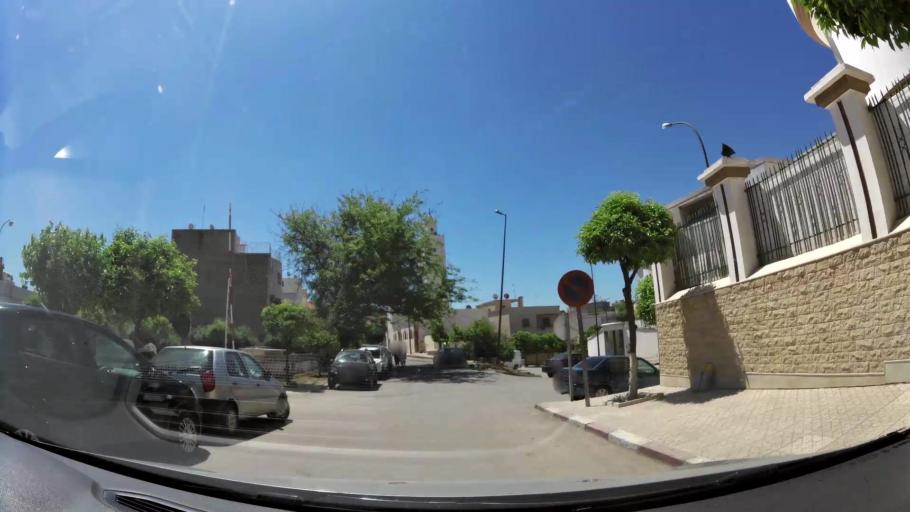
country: MA
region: Meknes-Tafilalet
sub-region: Meknes
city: Meknes
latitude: 33.8913
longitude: -5.5468
